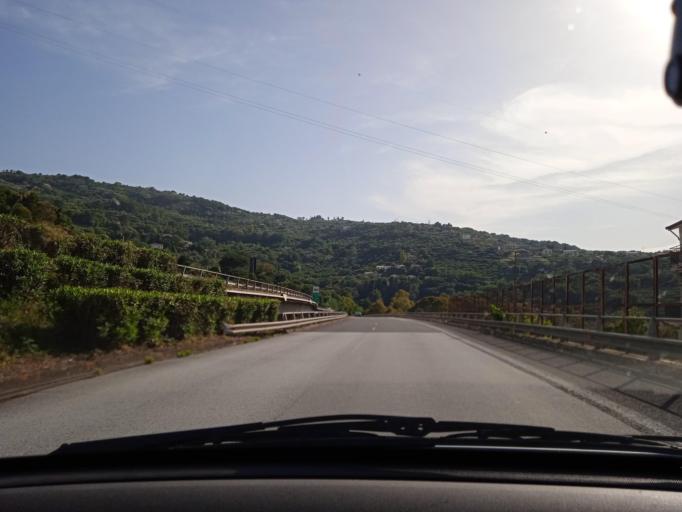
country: IT
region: Sicily
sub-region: Messina
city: Capo d'Orlando
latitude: 38.1499
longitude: 14.7662
